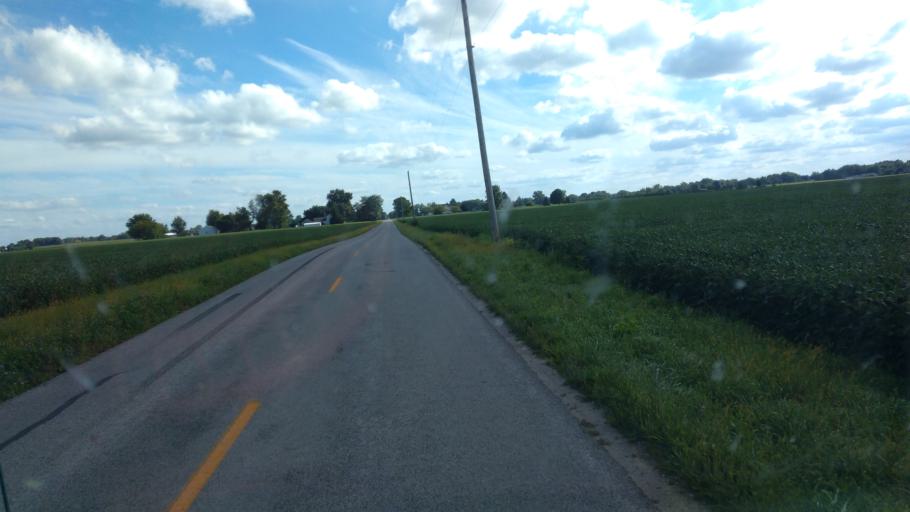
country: US
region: Ohio
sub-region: Sandusky County
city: Mount Carmel
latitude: 41.2827
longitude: -82.9557
